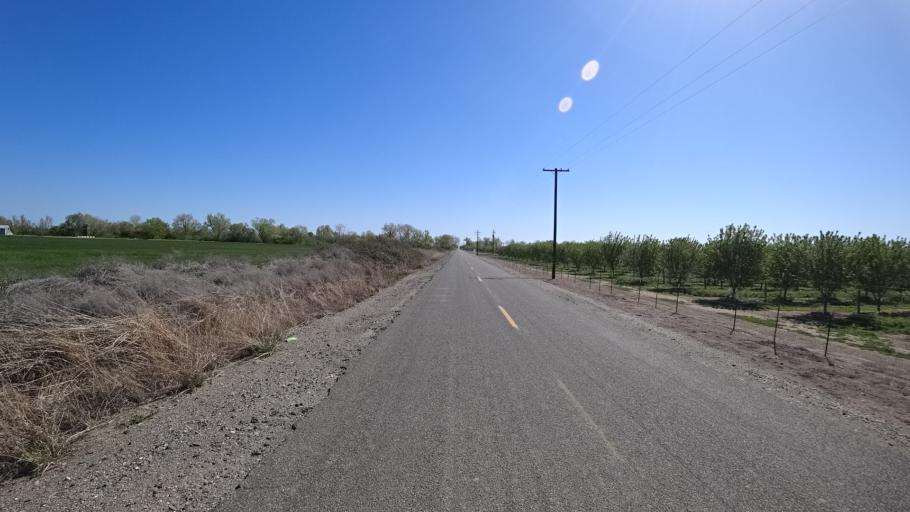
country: US
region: California
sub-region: Glenn County
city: Orland
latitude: 39.6972
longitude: -122.2311
